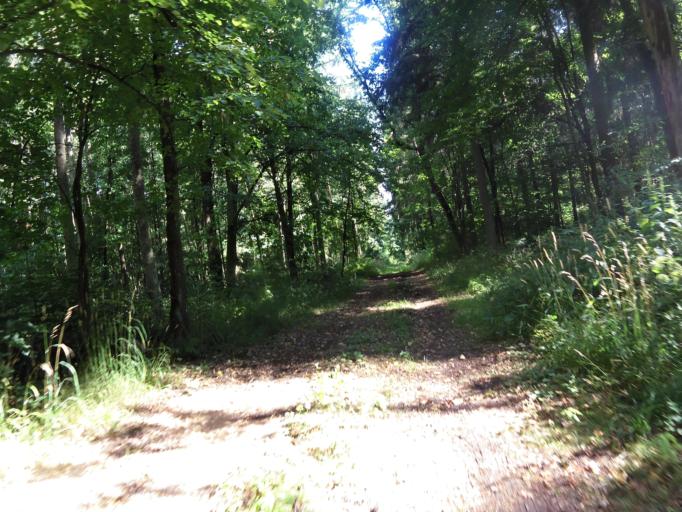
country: DE
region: Bavaria
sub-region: Regierungsbezirk Unterfranken
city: Gadheim
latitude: 49.8402
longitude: 9.9135
